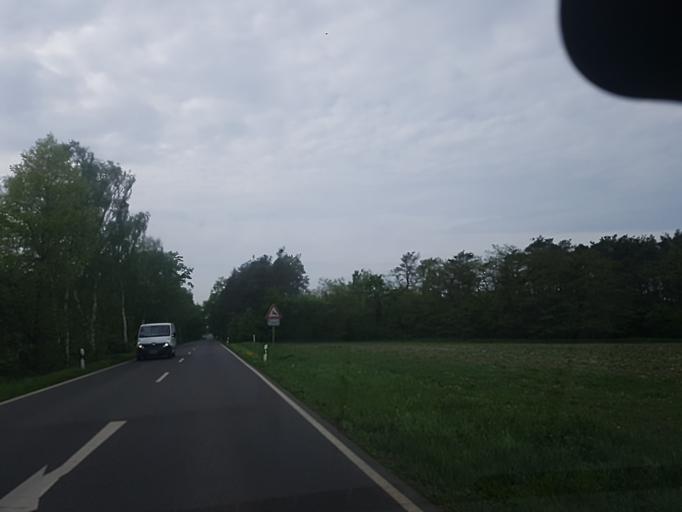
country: DE
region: Brandenburg
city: Finsterwalde
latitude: 51.6158
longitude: 13.7522
